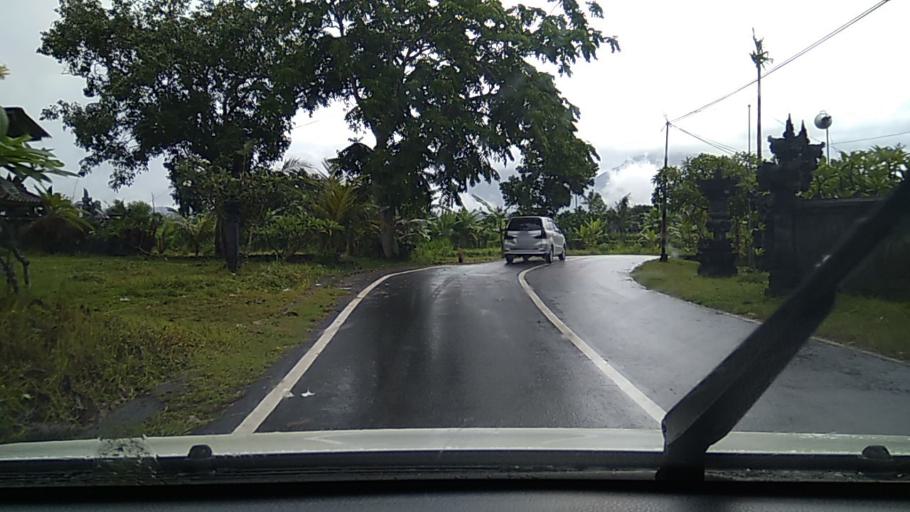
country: ID
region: Bali
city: Banjar Danginsema
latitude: -8.4644
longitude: 115.6223
